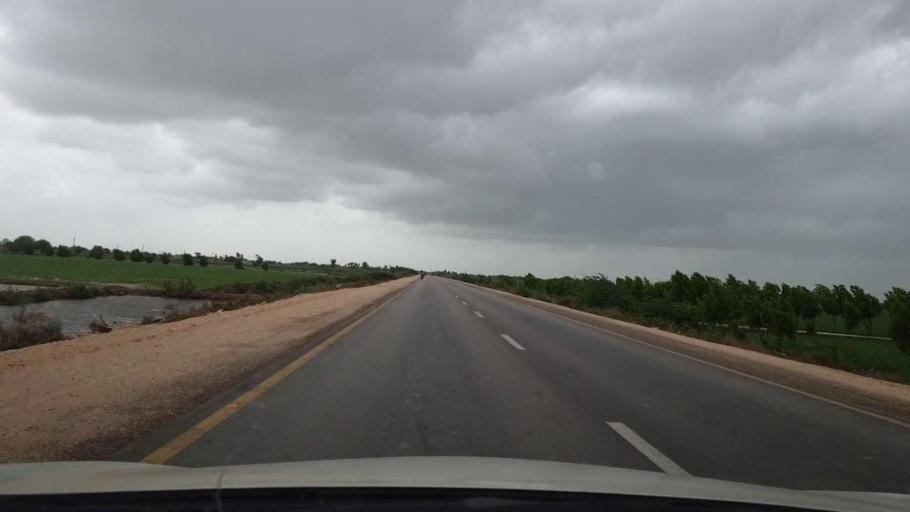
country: PK
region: Sindh
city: Mirpur Batoro
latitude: 24.6433
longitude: 68.4436
